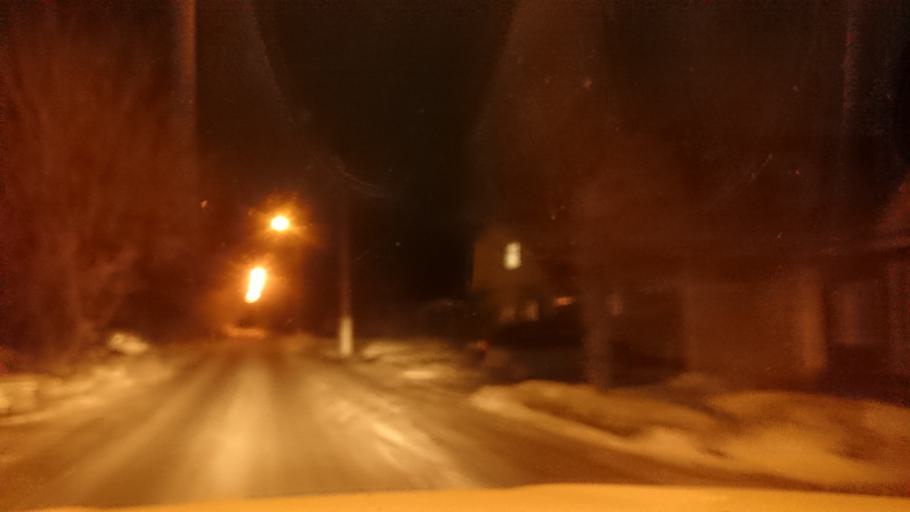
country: RU
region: Tula
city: Tula
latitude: 54.1861
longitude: 37.6327
